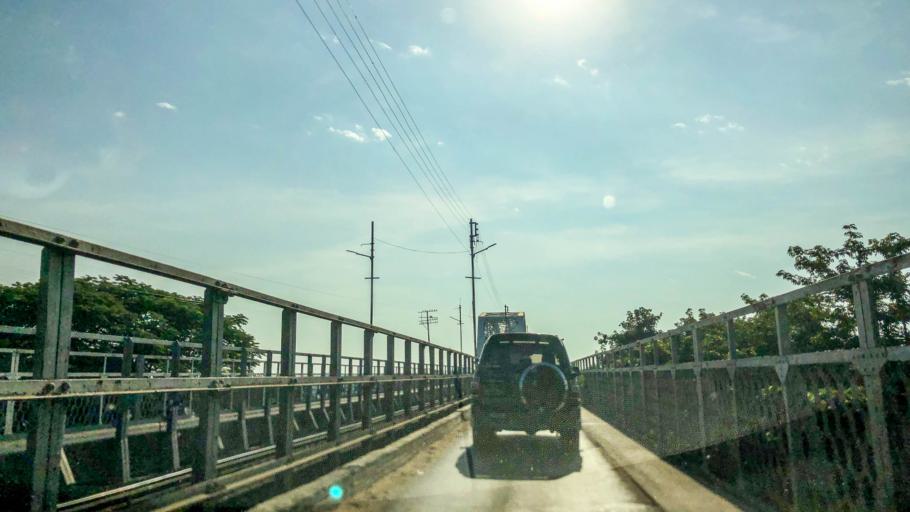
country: MM
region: Sagain
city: Sagaing
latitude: 21.8754
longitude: 95.9875
